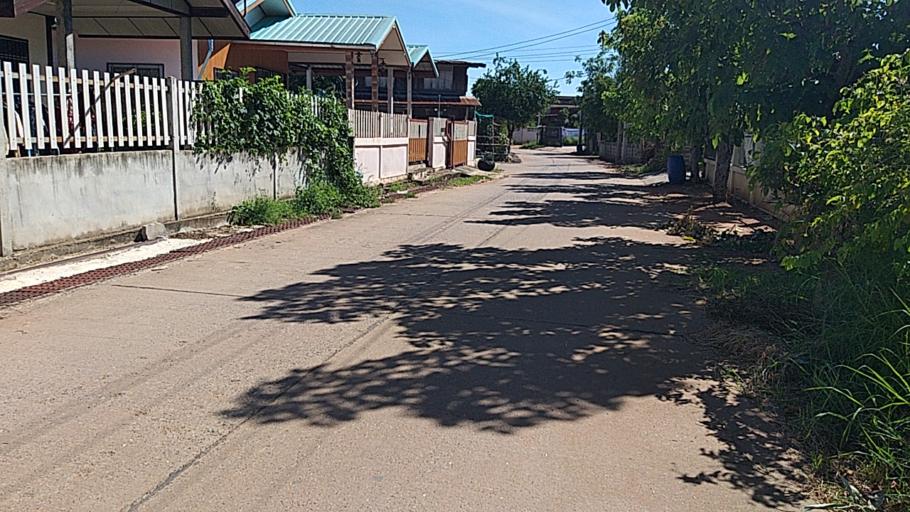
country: TH
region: Chaiyaphum
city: Ban Thaen
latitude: 16.4108
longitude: 102.3553
